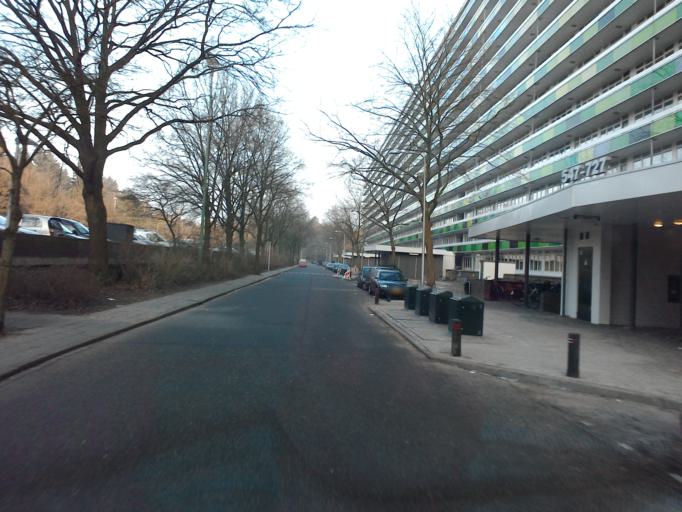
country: NL
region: Utrecht
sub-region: Gemeente Zeist
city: Zeist
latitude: 52.1022
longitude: 5.2341
